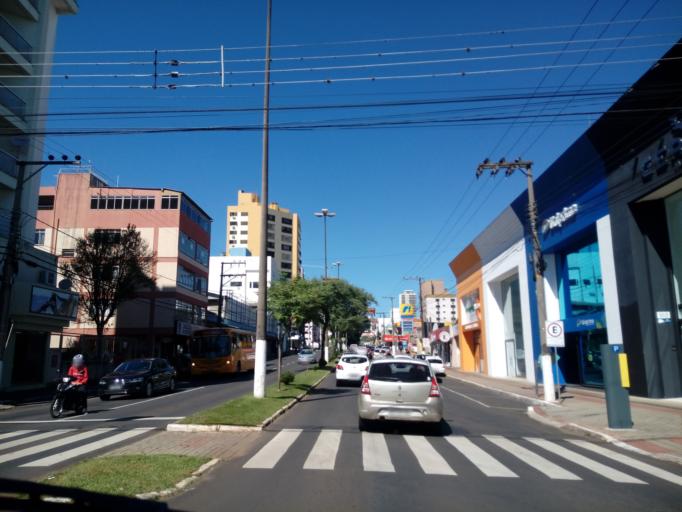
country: BR
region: Santa Catarina
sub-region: Chapeco
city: Chapeco
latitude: -27.1008
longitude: -52.6175
